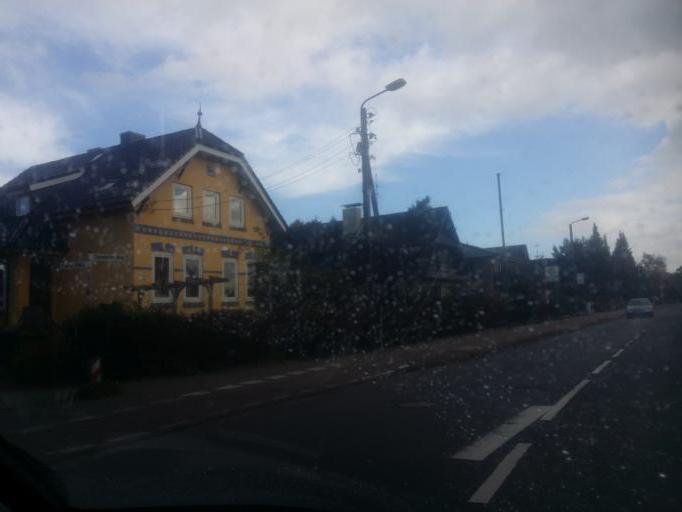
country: DE
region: Schleswig-Holstein
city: Pinneberg
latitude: 53.6503
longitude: 9.7764
